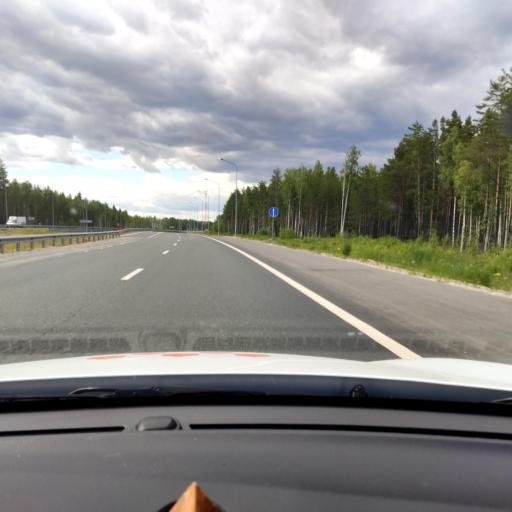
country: RU
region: Mariy-El
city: Surok
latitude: 56.4343
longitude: 48.1219
